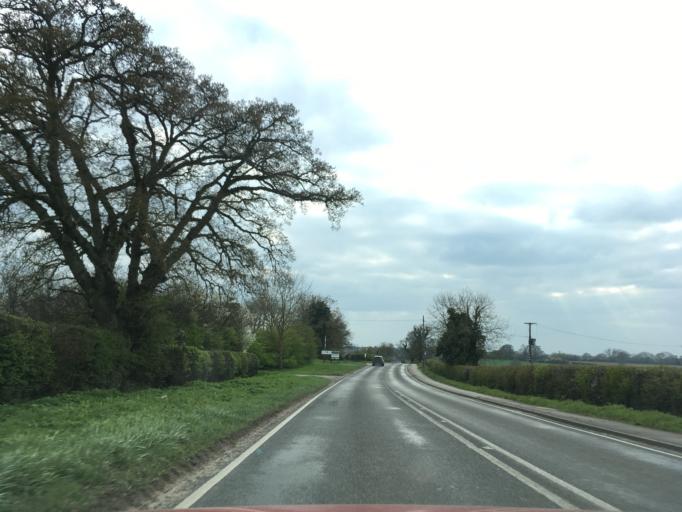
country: GB
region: England
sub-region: Oxfordshire
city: North Leigh
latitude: 51.8035
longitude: -1.4505
